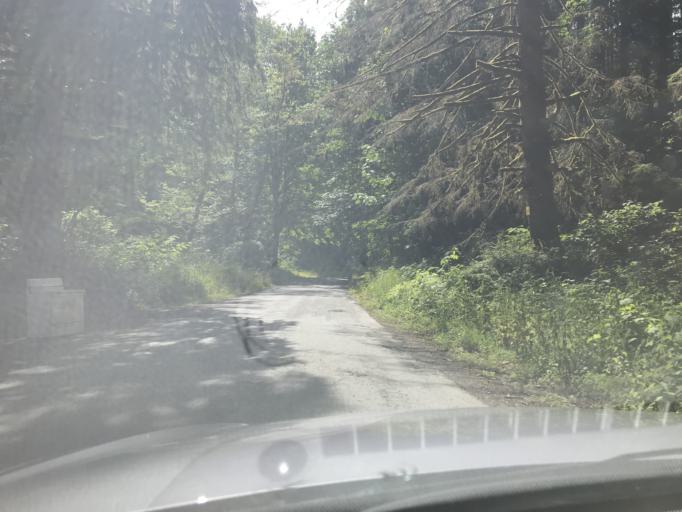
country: US
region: Washington
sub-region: King County
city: Hobart
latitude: 47.4149
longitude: -121.9223
